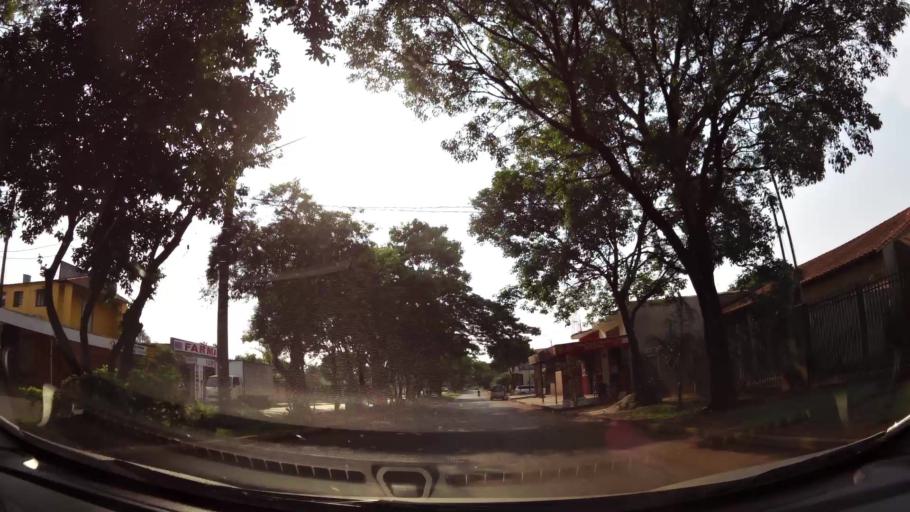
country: PY
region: Alto Parana
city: Ciudad del Este
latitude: -25.4848
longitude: -54.6637
